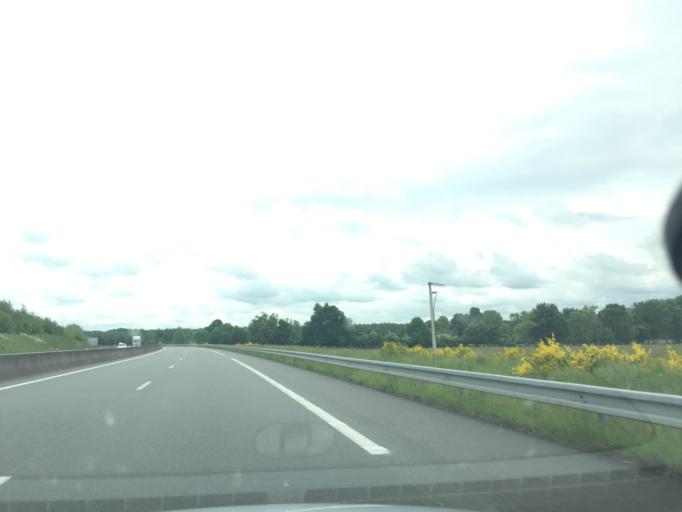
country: FR
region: Pays de la Loire
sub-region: Departement de la Sarthe
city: Luceau
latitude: 47.6684
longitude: 0.3749
